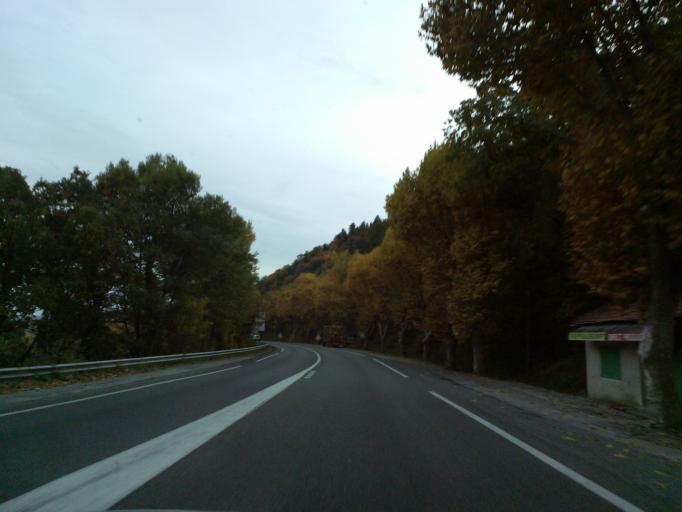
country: FR
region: Provence-Alpes-Cote d'Azur
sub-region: Departement des Alpes-de-Haute-Provence
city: Sisteron
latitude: 44.1729
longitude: 5.9483
